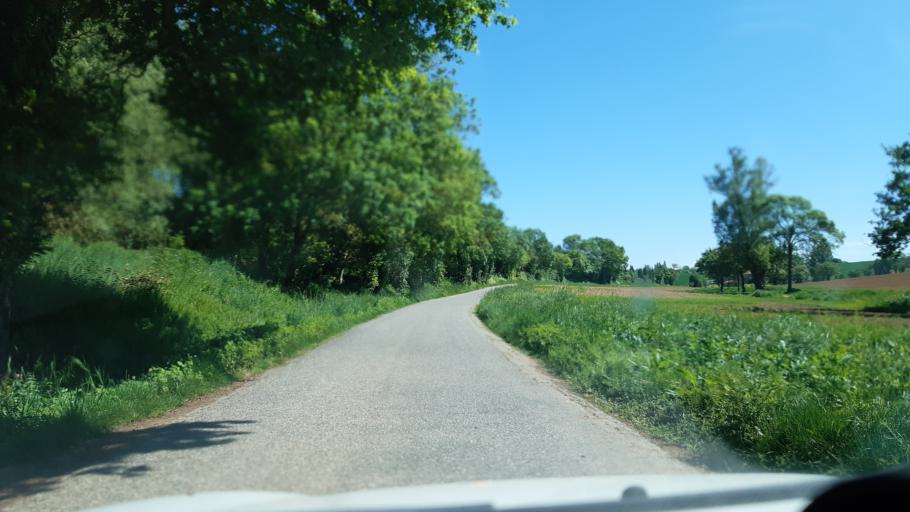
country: FR
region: Midi-Pyrenees
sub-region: Departement du Gers
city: Samatan
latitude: 43.5251
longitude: 0.9858
